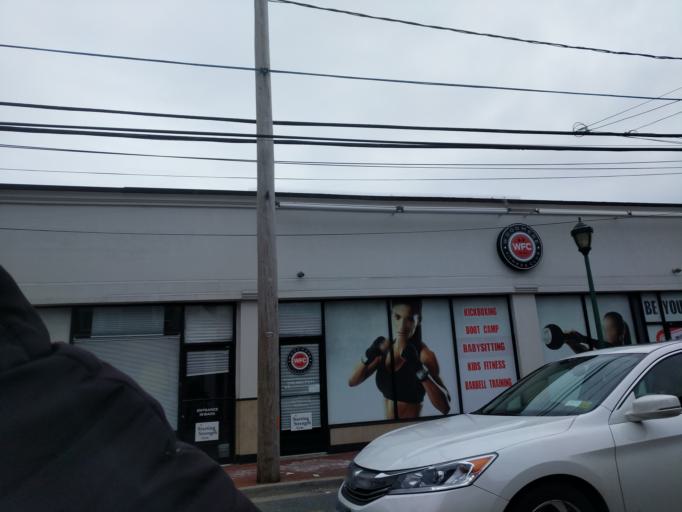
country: US
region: New York
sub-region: Nassau County
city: Woodmere
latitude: 40.6316
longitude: -73.7073
